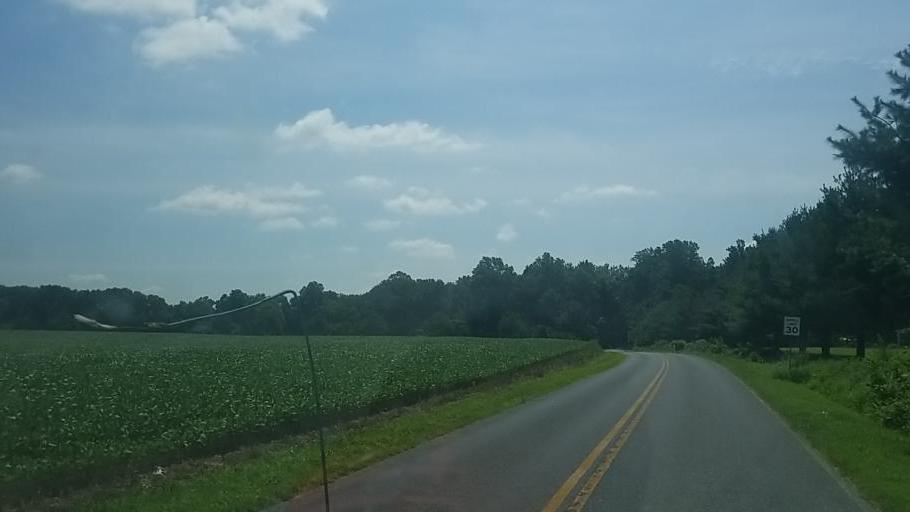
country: US
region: Maryland
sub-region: Caroline County
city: Ridgely
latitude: 38.9122
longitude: -75.9370
